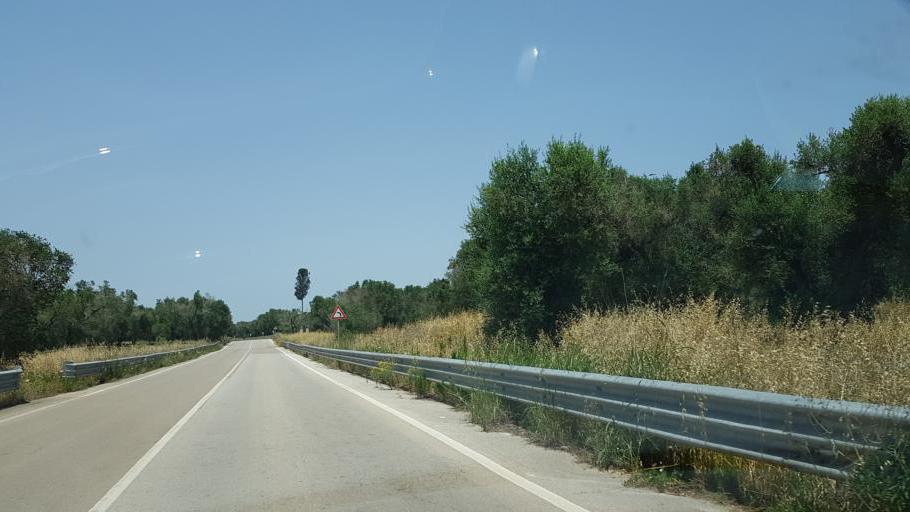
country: IT
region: Apulia
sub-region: Provincia di Brindisi
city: San Pancrazio Salentino
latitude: 40.4894
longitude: 17.8336
